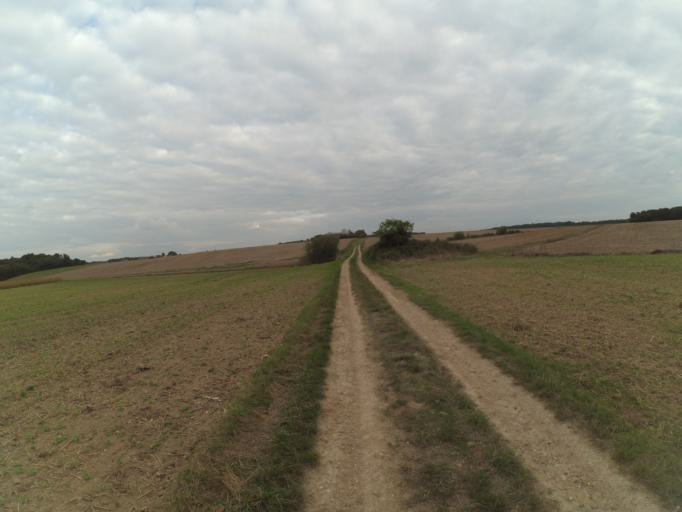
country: FR
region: Centre
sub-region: Departement d'Indre-et-Loire
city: Reugny
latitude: 47.4784
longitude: 0.9164
